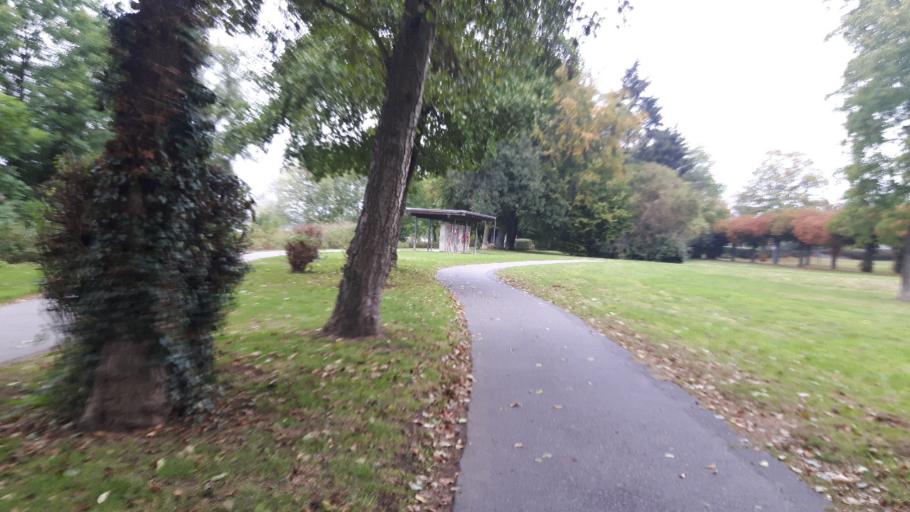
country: DE
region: North Rhine-Westphalia
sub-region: Regierungsbezirk Koln
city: Konigswinter
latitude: 50.6904
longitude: 7.1785
